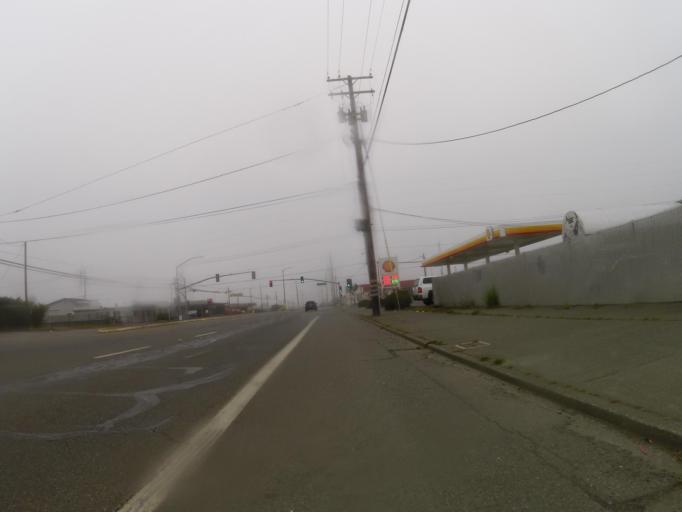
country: US
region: California
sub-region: Del Norte County
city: Crescent City
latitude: 41.7682
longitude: -124.1991
